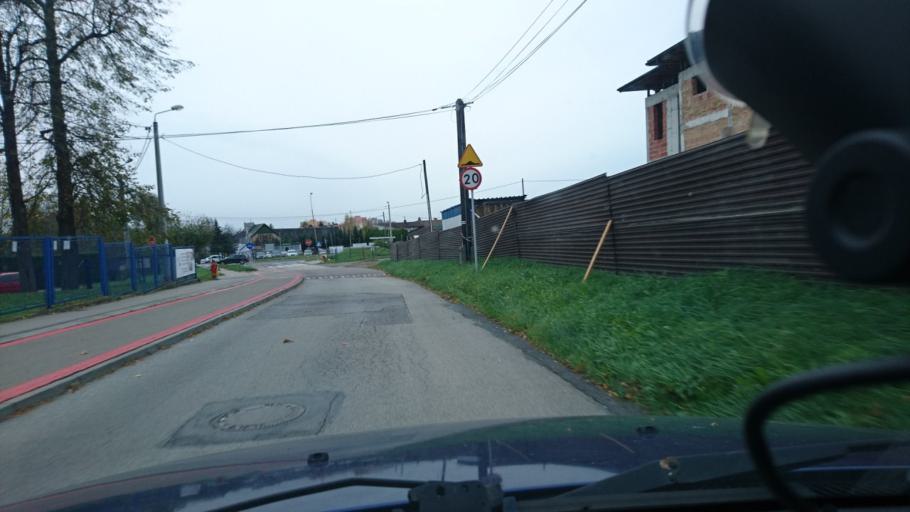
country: PL
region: Silesian Voivodeship
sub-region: Bielsko-Biala
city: Bielsko-Biala
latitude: 49.8084
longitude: 19.0159
